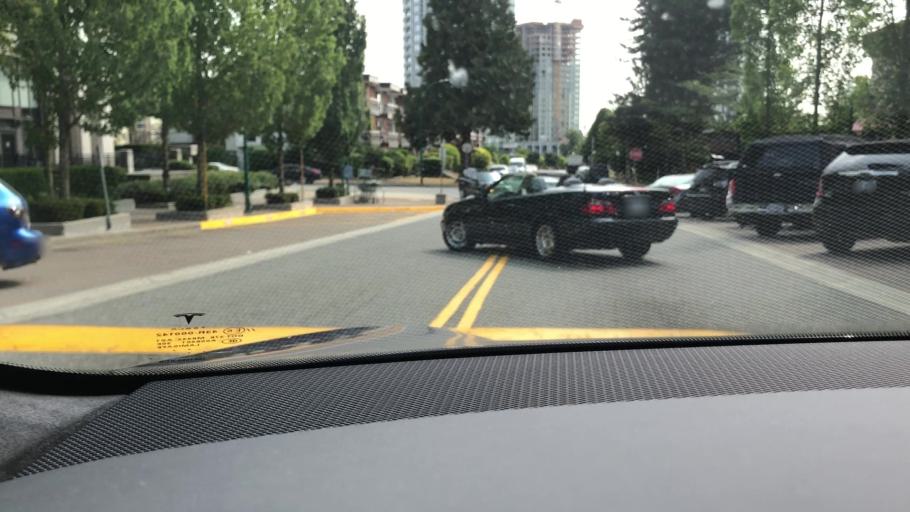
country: CA
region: British Columbia
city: New Westminster
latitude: 49.2193
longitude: -122.9558
